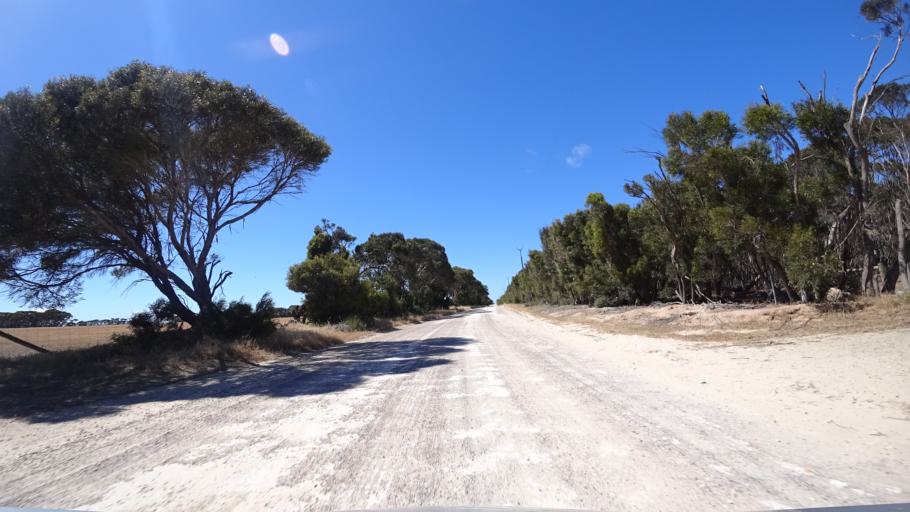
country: AU
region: South Australia
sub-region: Kangaroo Island
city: Kingscote
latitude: -35.7655
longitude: 137.7596
